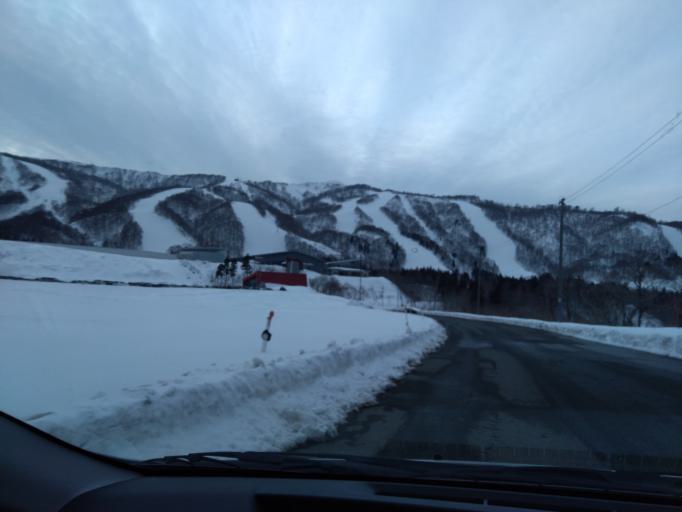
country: JP
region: Iwate
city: Kitakami
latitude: 39.2368
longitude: 140.9098
